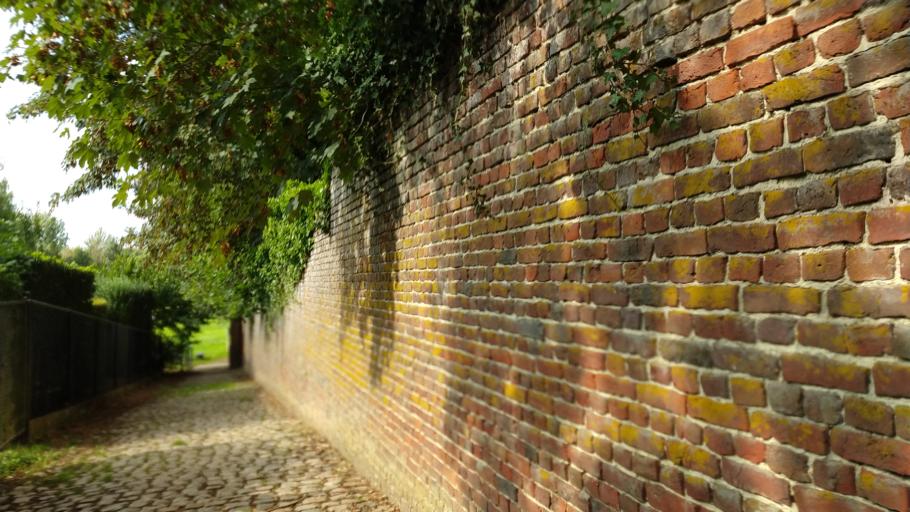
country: BE
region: Flanders
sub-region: Provincie Vlaams-Brabant
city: Boutersem
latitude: 50.8311
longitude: 4.8348
